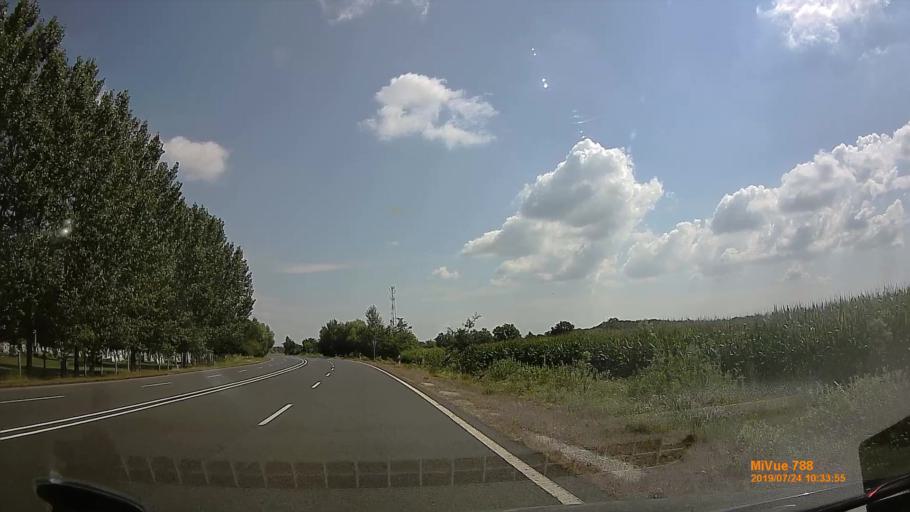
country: HU
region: Szabolcs-Szatmar-Bereg
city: Tarpa
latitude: 48.1593
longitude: 22.5583
